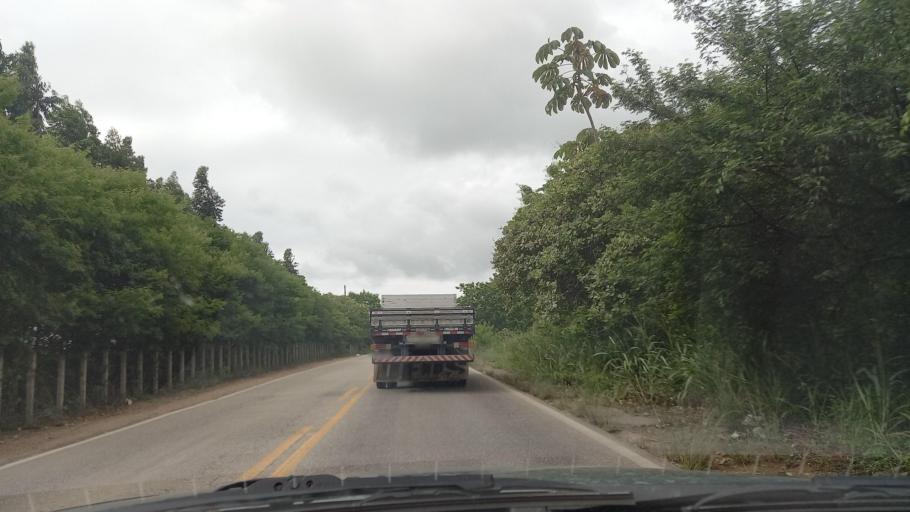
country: BR
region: Pernambuco
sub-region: Canhotinho
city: Canhotinho
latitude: -8.8609
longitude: -36.1808
